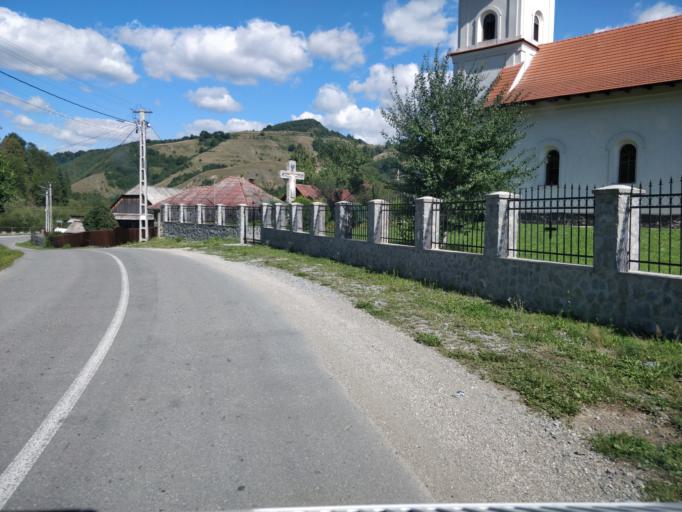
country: RO
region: Cluj
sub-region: Comuna Sacueu
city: Sacuieu
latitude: 46.8227
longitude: 22.8871
